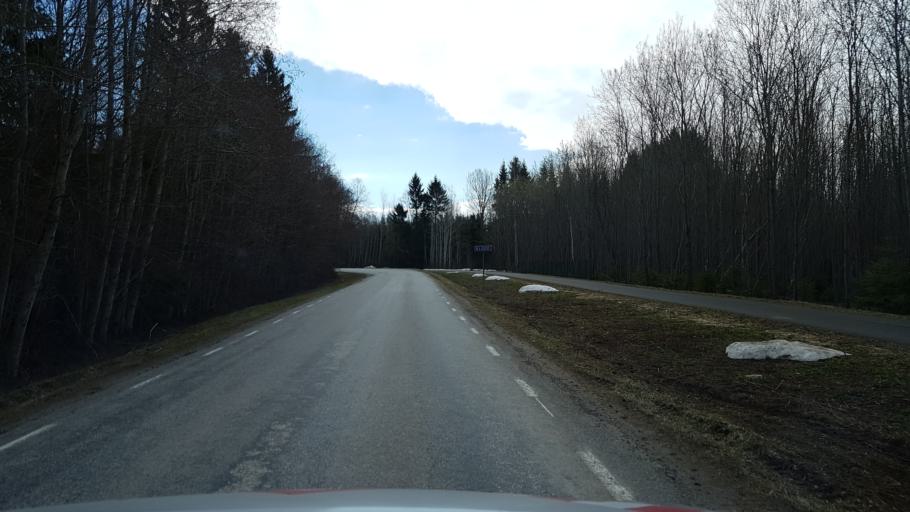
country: EE
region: Laeaene-Virumaa
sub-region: Haljala vald
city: Haljala
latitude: 59.3922
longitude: 26.2905
